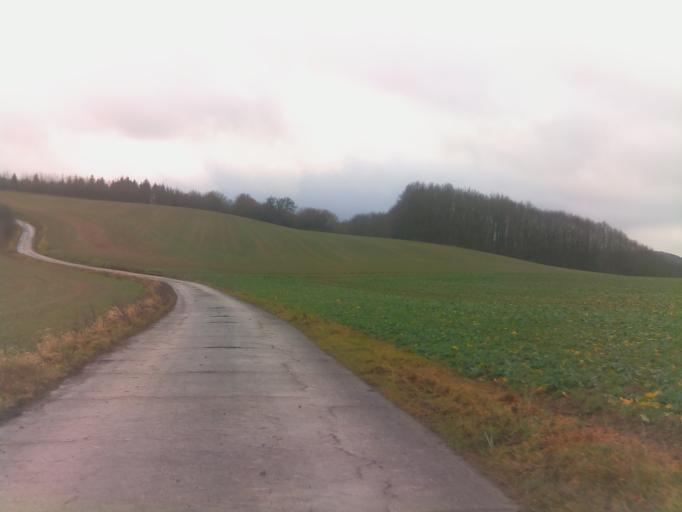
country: DE
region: Rheinland-Pfalz
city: Wurzweiler
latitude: 49.6508
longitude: 7.8668
